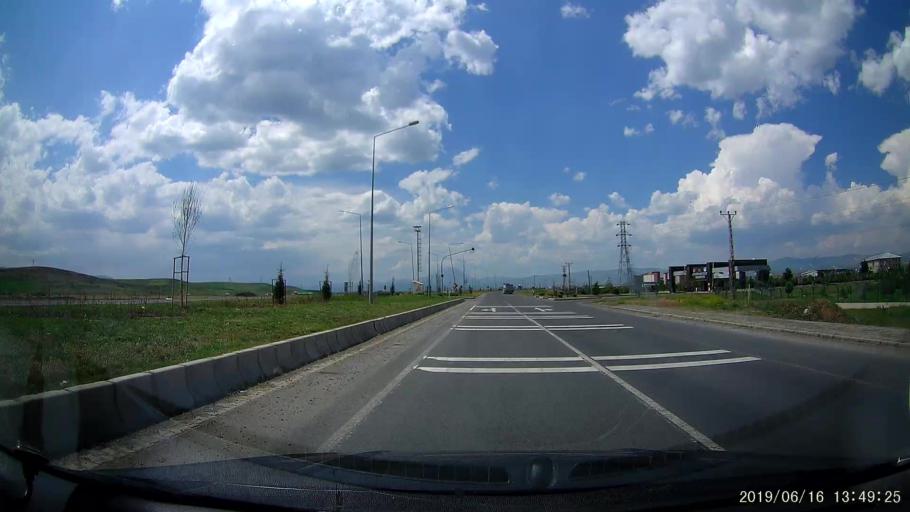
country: TR
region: Agri
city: Agri
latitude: 39.7171
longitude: 42.9911
